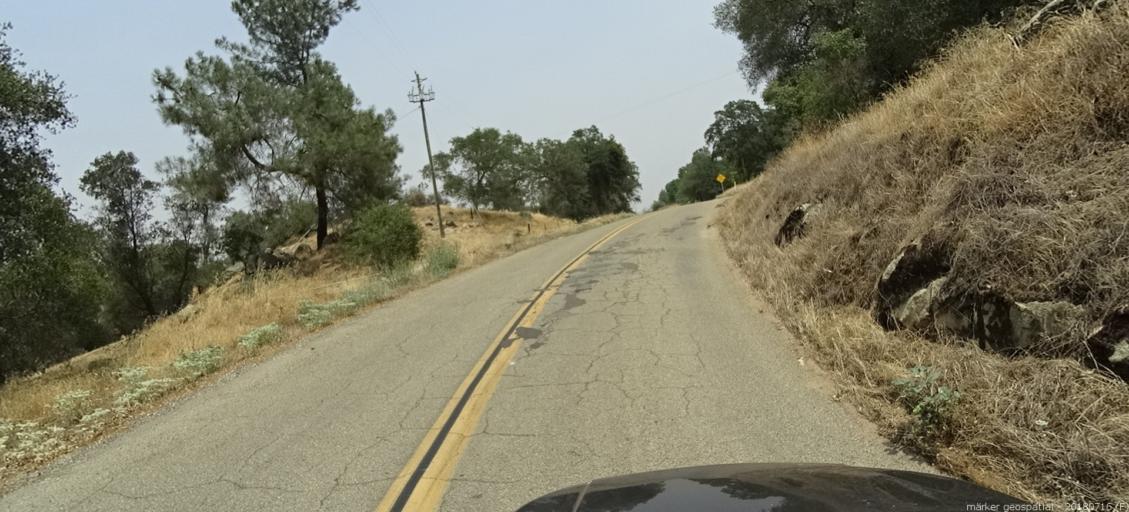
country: US
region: California
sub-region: Madera County
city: Yosemite Lakes
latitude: 37.2186
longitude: -119.8756
